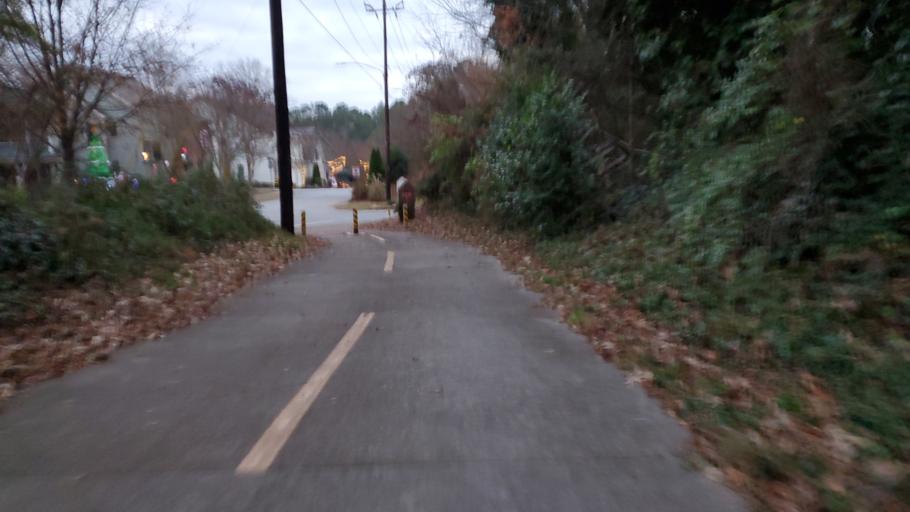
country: US
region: Georgia
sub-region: DeKalb County
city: Scottdale
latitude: 33.7804
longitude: -84.2632
